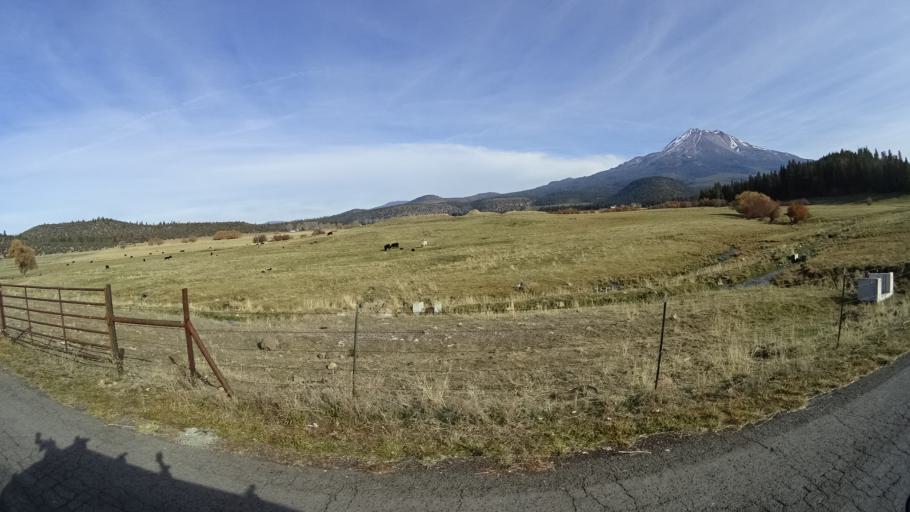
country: US
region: California
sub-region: Siskiyou County
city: Weed
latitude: 41.4538
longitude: -122.3836
